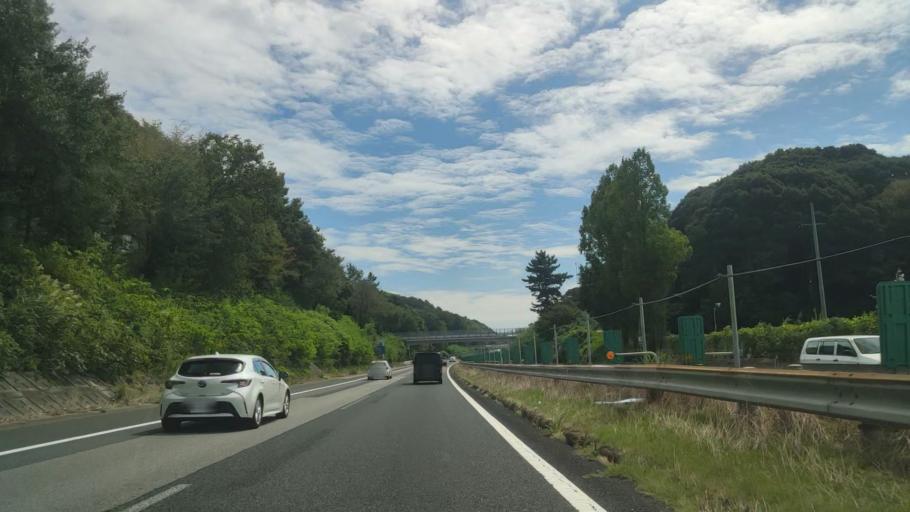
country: JP
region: Aichi
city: Okazaki
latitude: 34.9982
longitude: 137.1800
